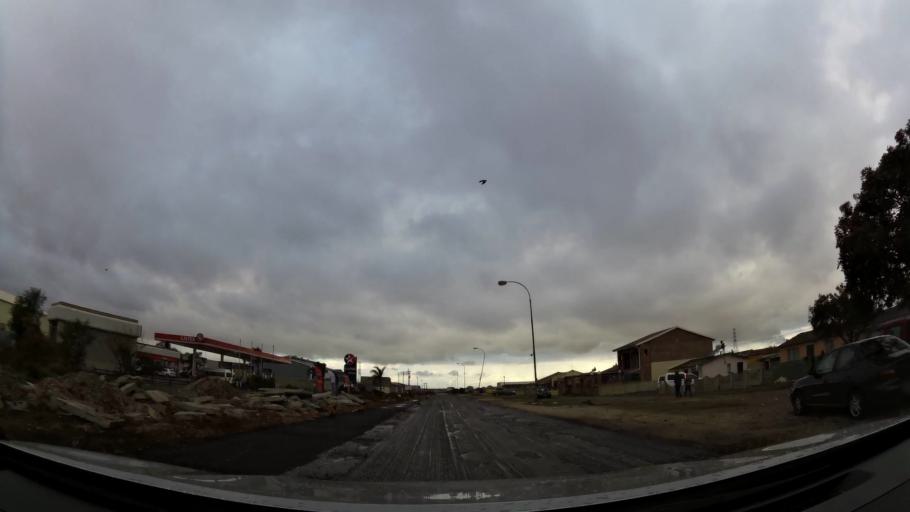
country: ZA
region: Eastern Cape
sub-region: Nelson Mandela Bay Metropolitan Municipality
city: Port Elizabeth
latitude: -33.8951
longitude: 25.5457
